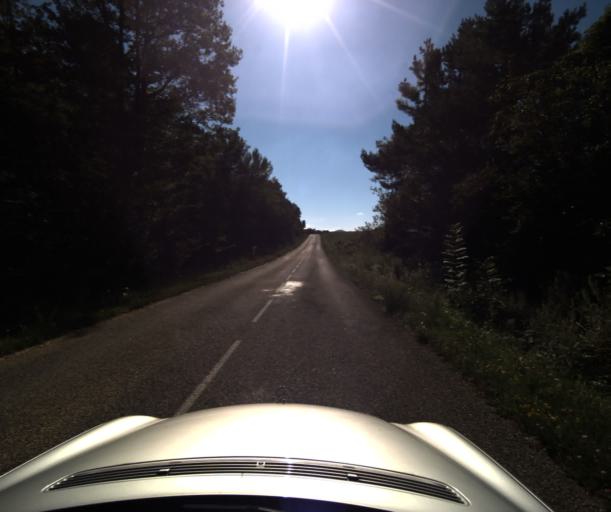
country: FR
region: Midi-Pyrenees
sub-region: Departement de l'Ariege
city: Belesta
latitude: 42.9707
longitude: 1.9301
